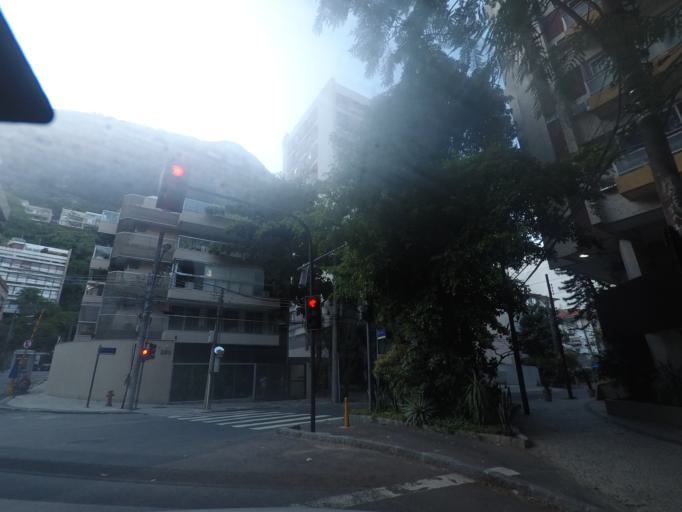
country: BR
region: Rio de Janeiro
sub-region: Rio De Janeiro
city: Rio de Janeiro
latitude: -22.9663
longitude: -43.2025
